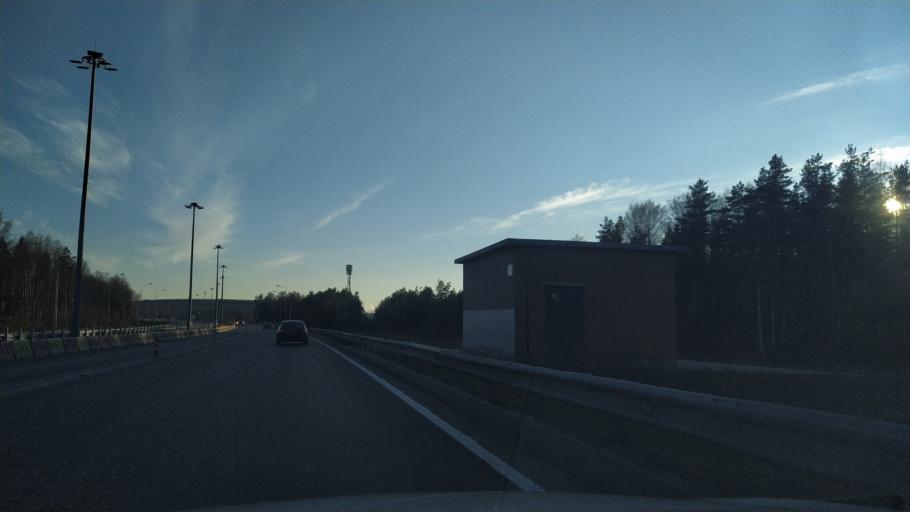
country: RU
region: St.-Petersburg
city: Levashovo
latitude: 60.0814
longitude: 30.1952
